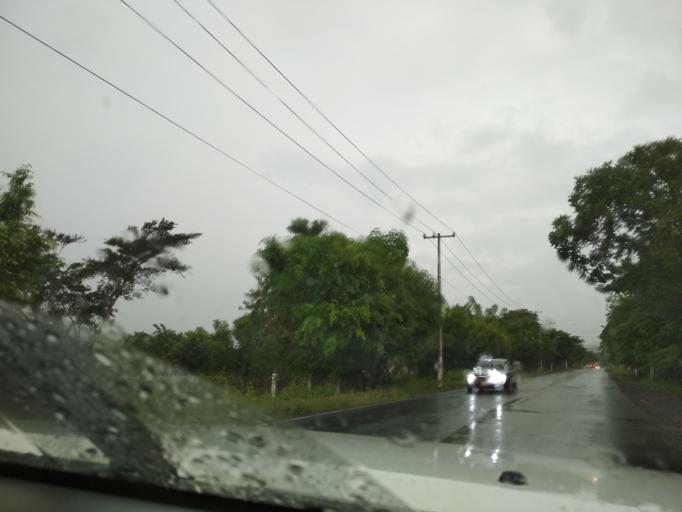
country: MX
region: Veracruz
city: Santiago Tuxtla
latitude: 18.4519
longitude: -95.3144
